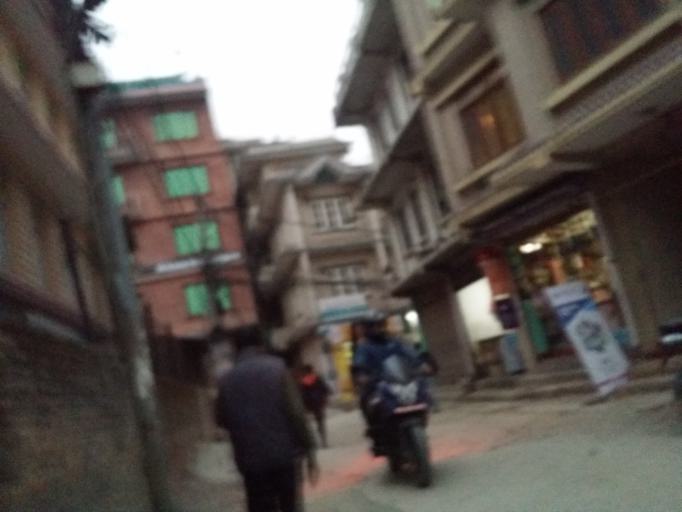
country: NP
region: Central Region
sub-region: Bagmati Zone
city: Kathmandu
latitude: 27.7028
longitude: 85.3493
